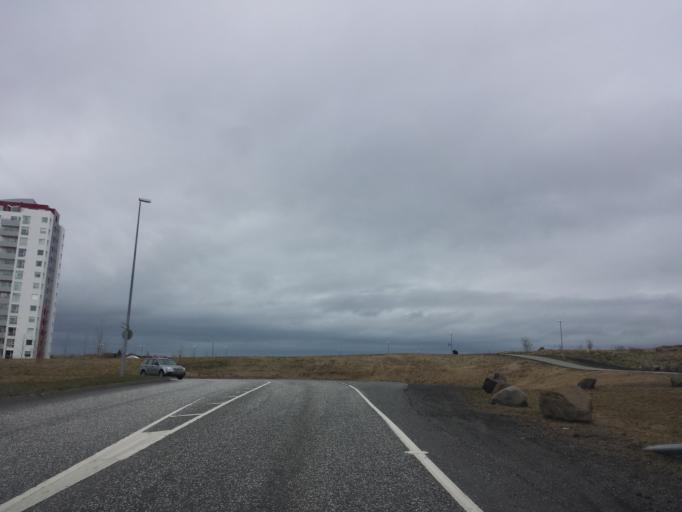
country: IS
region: Capital Region
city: Reykjavik
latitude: 64.0887
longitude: -21.8358
